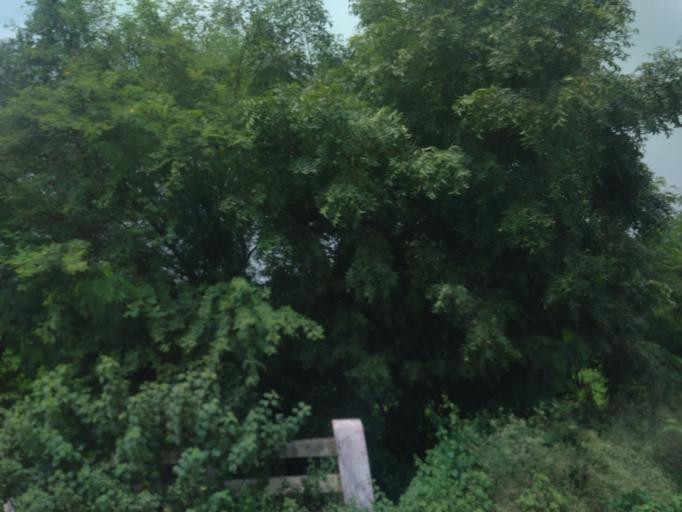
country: IN
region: Telangana
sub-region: Warangal
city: Jangaon
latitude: 17.6594
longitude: 79.0768
